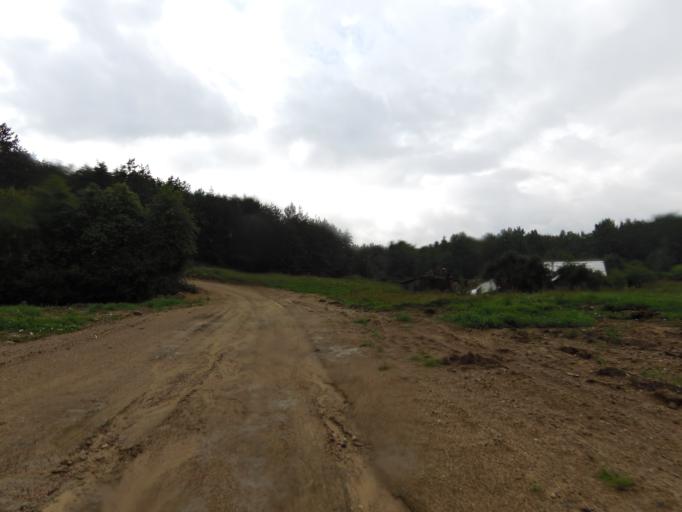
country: LT
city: Grigiskes
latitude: 54.7131
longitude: 25.1119
